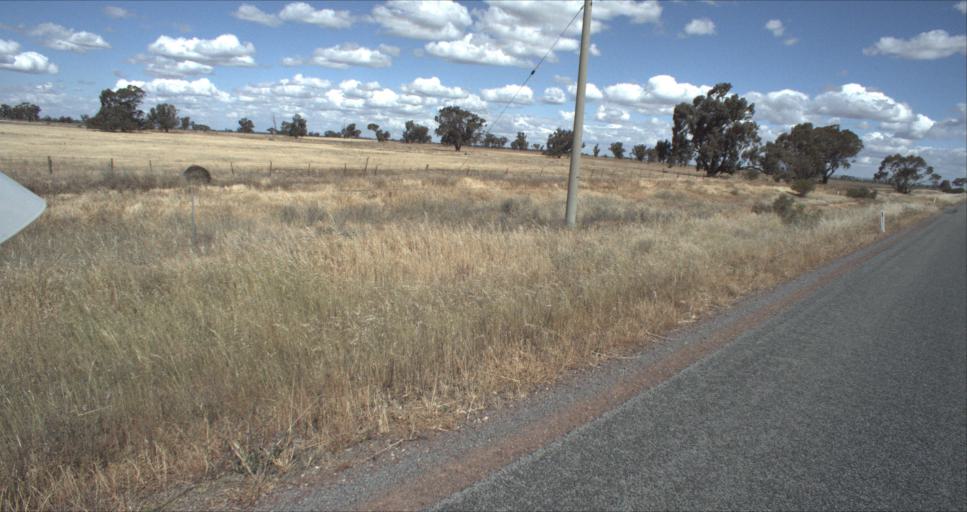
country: AU
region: New South Wales
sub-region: Leeton
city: Leeton
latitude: -34.4871
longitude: 146.2480
